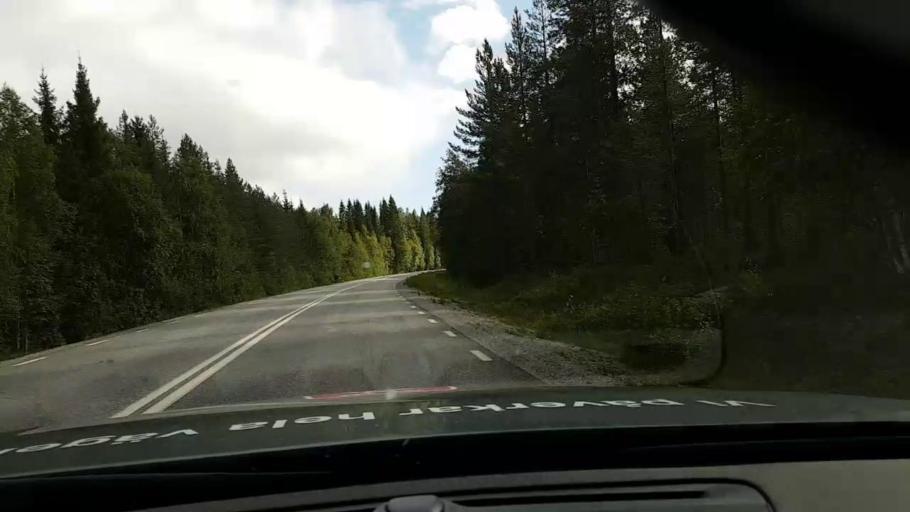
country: SE
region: Vaesternorrland
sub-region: OErnskoeldsviks Kommun
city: Bredbyn
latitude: 63.6326
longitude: 17.9097
